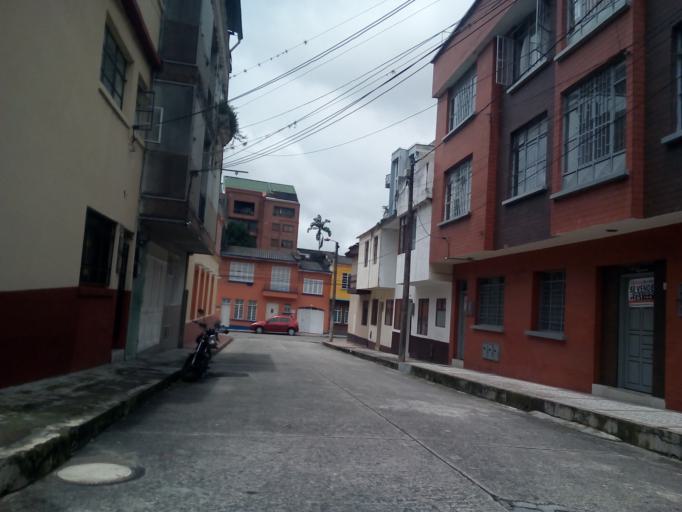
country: CO
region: Tolima
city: Ibague
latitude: 4.4481
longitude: -75.2465
